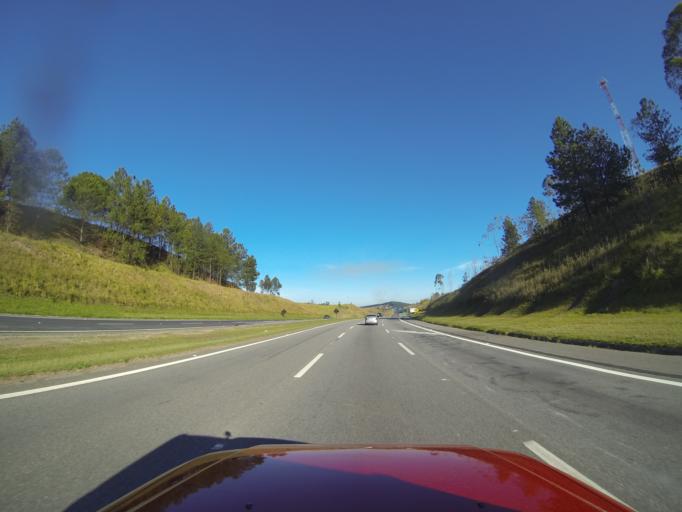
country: BR
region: Sao Paulo
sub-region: Santa Isabel
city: Santa Isabel
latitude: -23.1899
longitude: -46.1898
